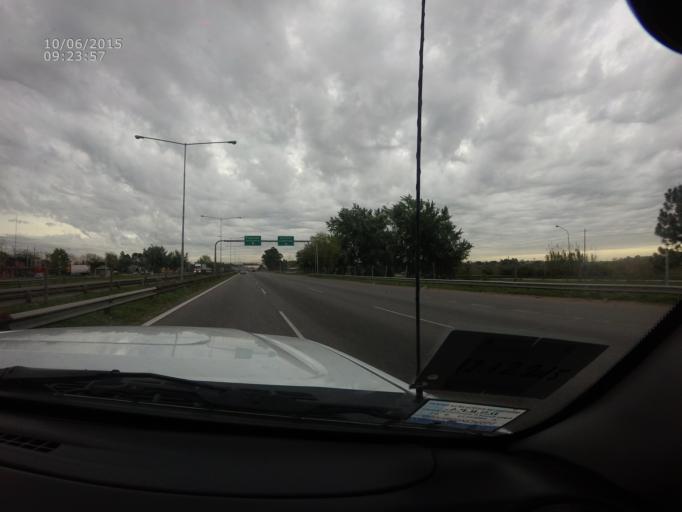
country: AR
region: Buenos Aires
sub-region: Partido de Campana
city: Campana
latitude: -34.1969
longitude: -58.9395
